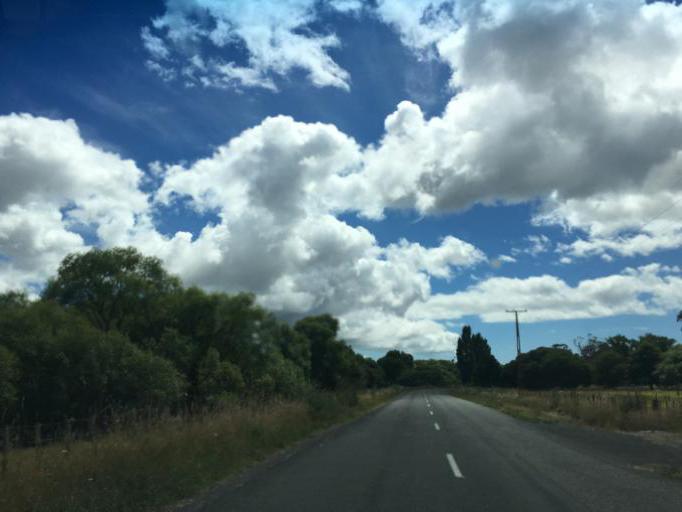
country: NZ
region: Hawke's Bay
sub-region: Hastings District
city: Hastings
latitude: -39.7504
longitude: 176.8762
